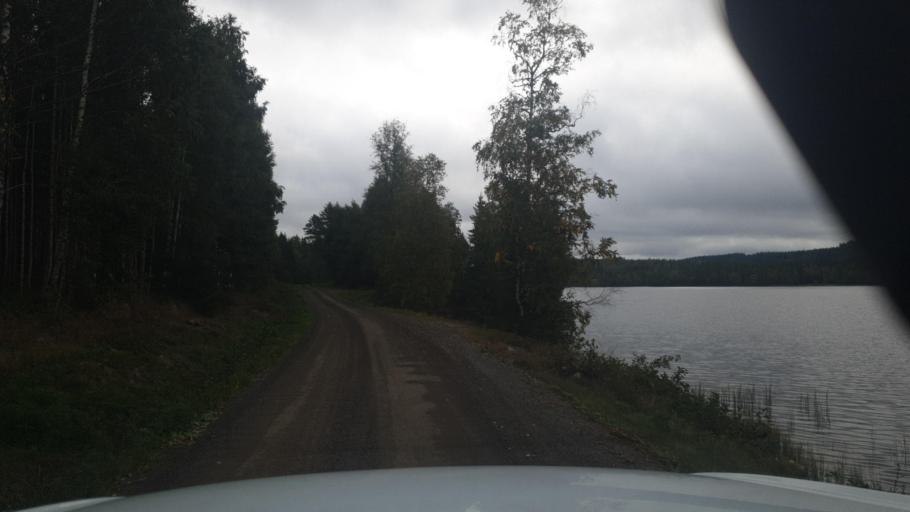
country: SE
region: Vaermland
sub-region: Arvika Kommun
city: Arvika
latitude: 59.8677
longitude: 12.8117
